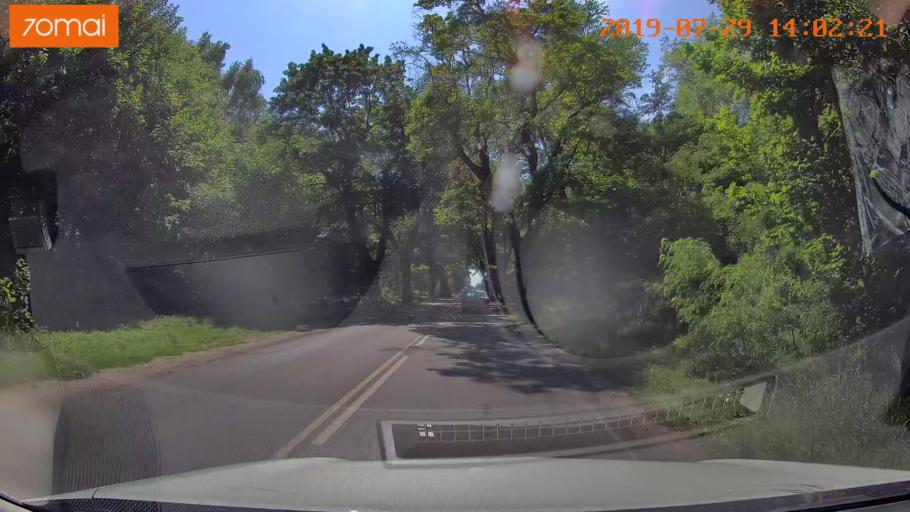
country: RU
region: Kaliningrad
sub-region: Gorod Kaliningrad
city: Baltiysk
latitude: 54.6636
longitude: 19.9163
